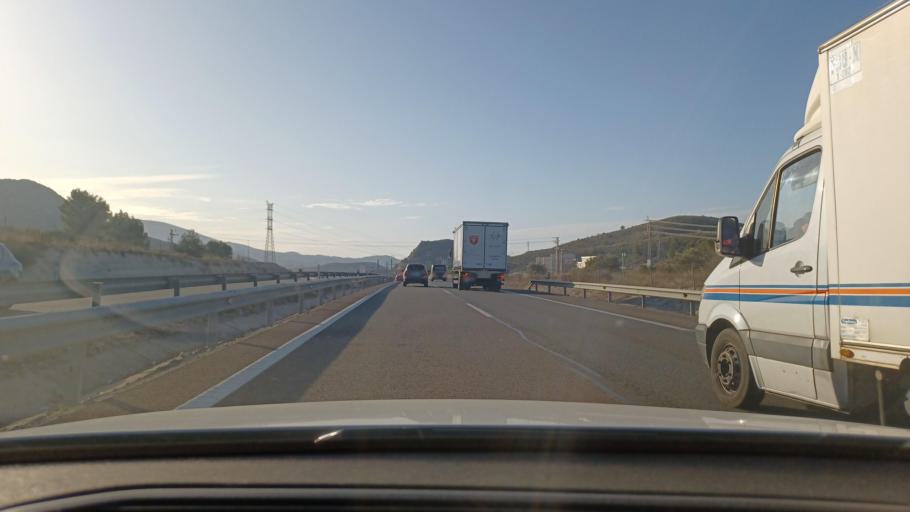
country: ES
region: Valencia
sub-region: Provincia de Alicante
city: Elda
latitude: 38.5027
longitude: -0.7921
